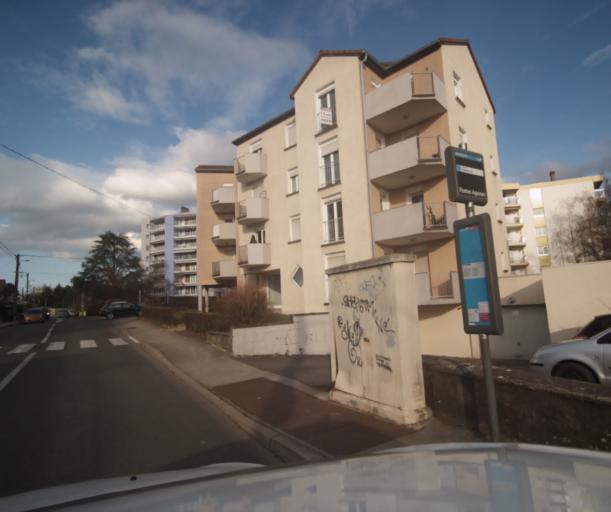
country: FR
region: Franche-Comte
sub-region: Departement du Doubs
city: Besancon
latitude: 47.2569
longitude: 6.0283
